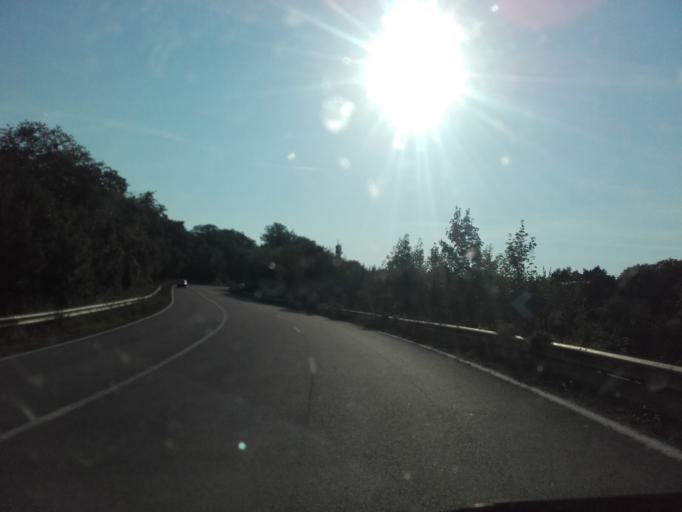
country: FR
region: Bourgogne
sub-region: Departement de l'Yonne
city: Venoy
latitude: 47.8130
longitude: 3.7065
